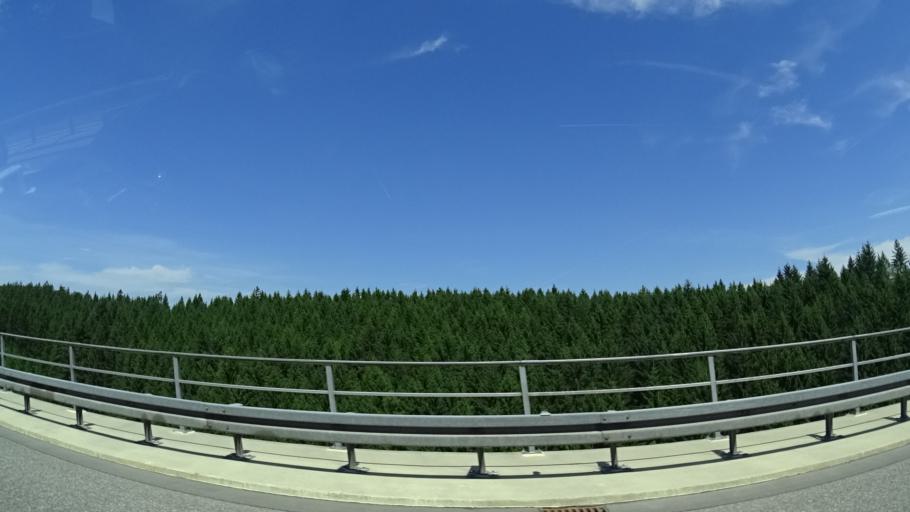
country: DE
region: Thuringia
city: Benshausen
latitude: 50.6106
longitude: 10.6317
